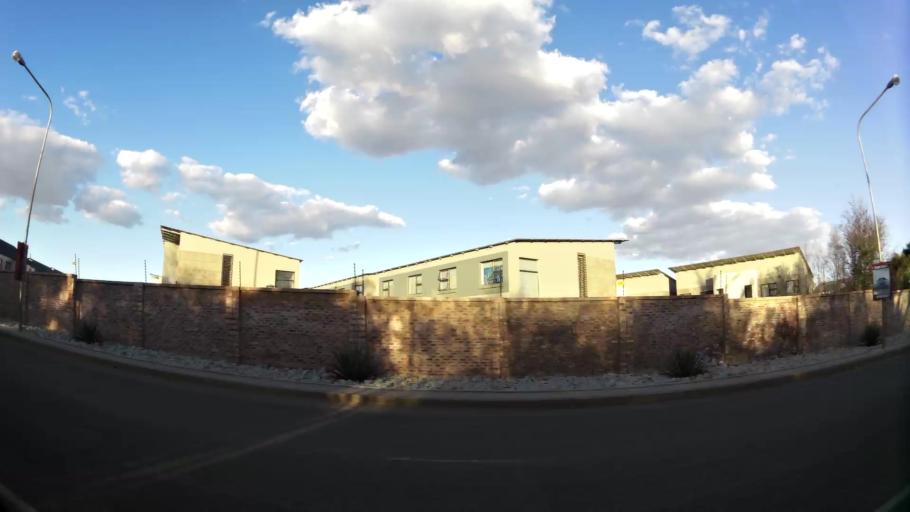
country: ZA
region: North-West
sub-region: Dr Kenneth Kaunda District Municipality
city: Potchefstroom
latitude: -26.6819
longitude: 27.1024
